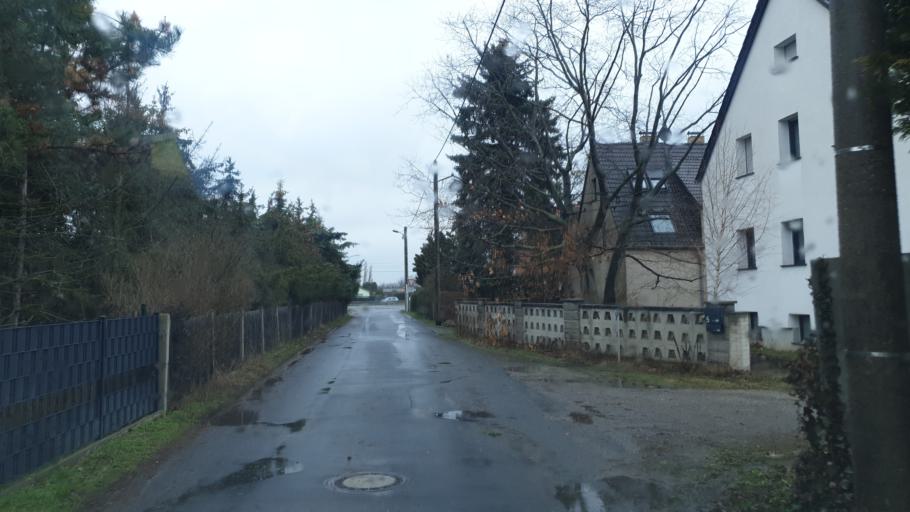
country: DE
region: Saxony
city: Thallwitz
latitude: 51.4660
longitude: 12.6786
